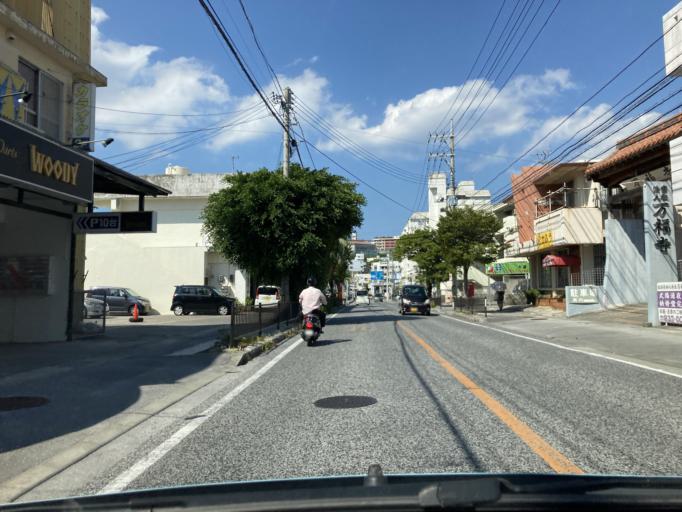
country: JP
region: Okinawa
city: Tomigusuku
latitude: 26.1941
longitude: 127.7061
